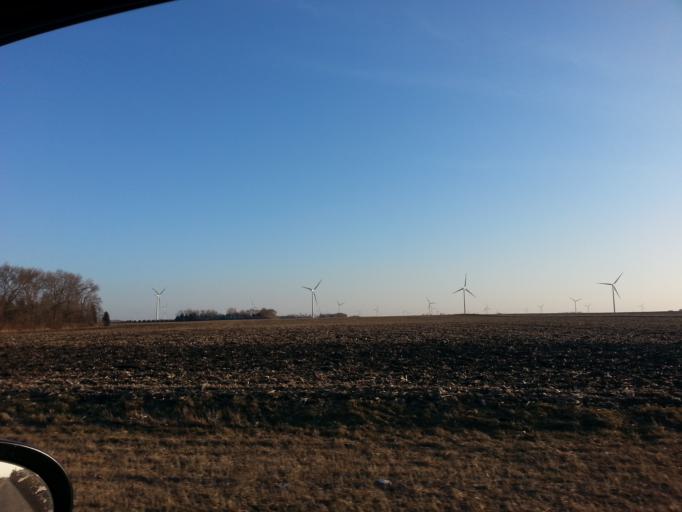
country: US
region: Iowa
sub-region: Worth County
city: Northwood
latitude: 43.4363
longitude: -93.0930
